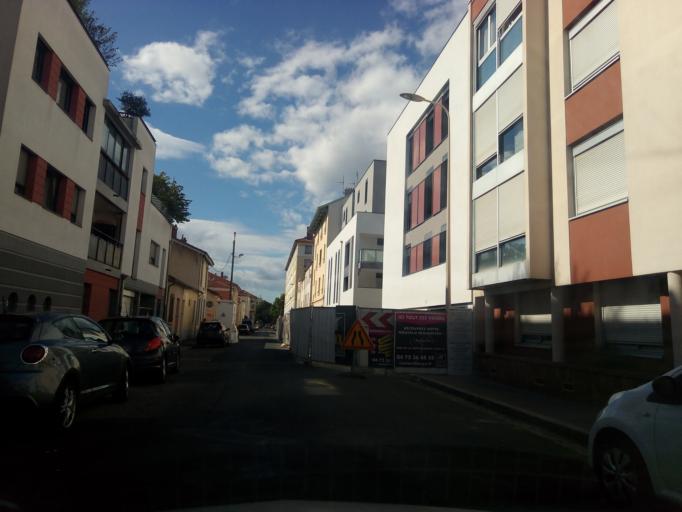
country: FR
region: Rhone-Alpes
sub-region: Departement du Rhone
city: Villeurbanne
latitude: 45.7513
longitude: 4.8873
